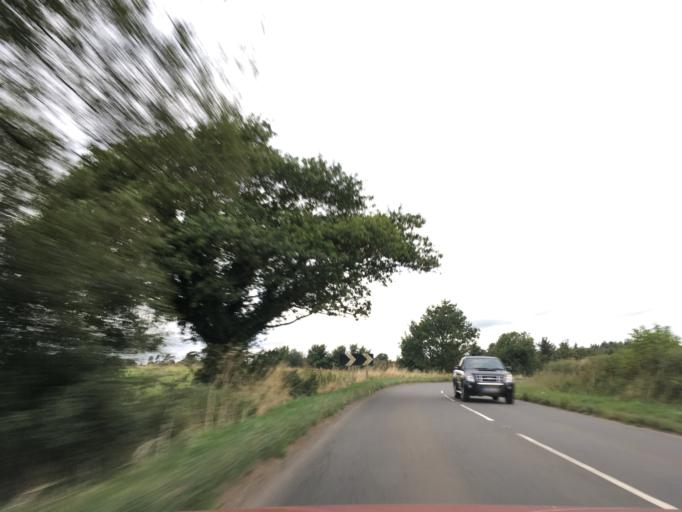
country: GB
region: England
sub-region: Wiltshire
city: Calne
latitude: 51.3925
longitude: -2.0428
